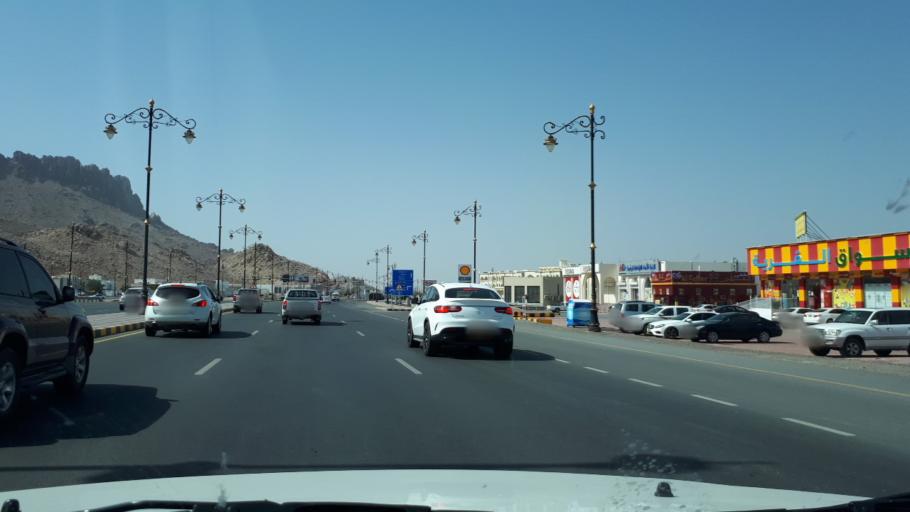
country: OM
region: Muhafazat ad Dakhiliyah
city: Nizwa
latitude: 22.9089
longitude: 57.5344
